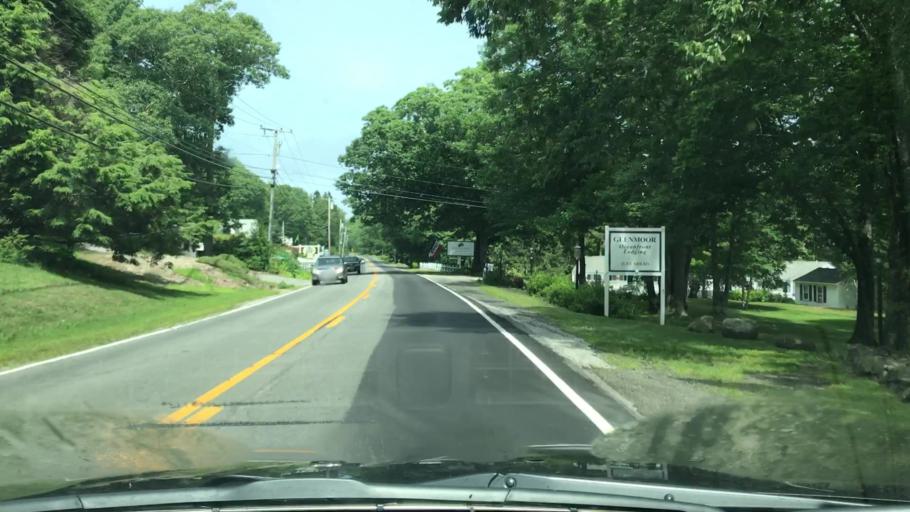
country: US
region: Maine
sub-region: Waldo County
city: Lincolnville
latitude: 44.2586
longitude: -69.0238
